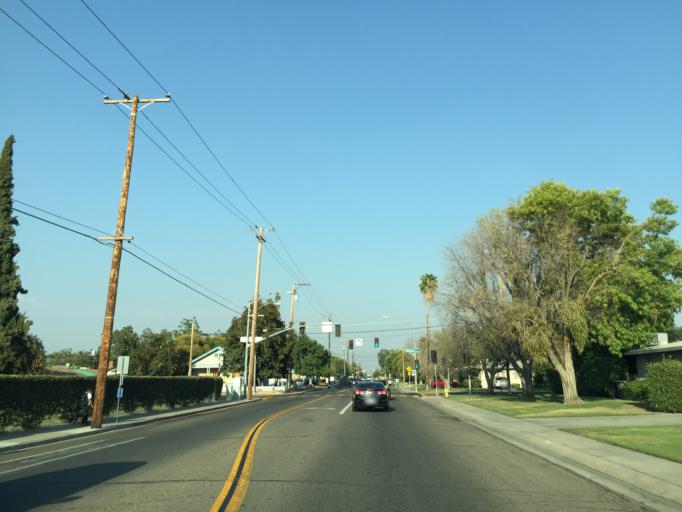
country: US
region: California
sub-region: Tulare County
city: Visalia
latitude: 36.3201
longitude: -119.2968
